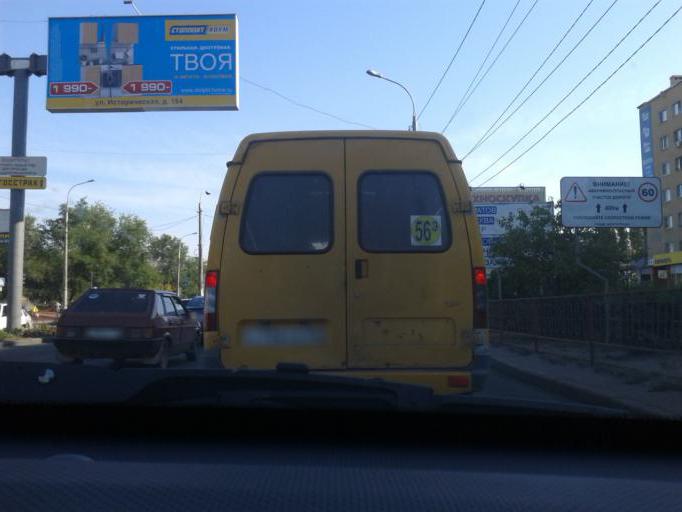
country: RU
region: Volgograd
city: Volgograd
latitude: 48.6748
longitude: 44.4439
